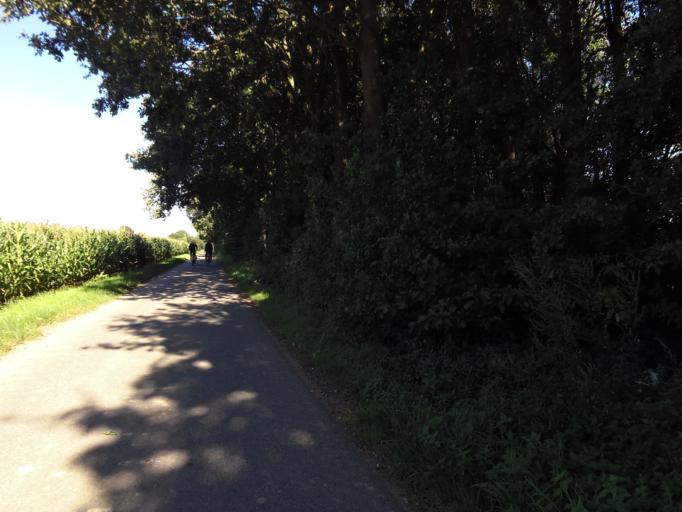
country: DE
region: North Rhine-Westphalia
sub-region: Regierungsbezirk Koln
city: Rheinbach
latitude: 50.6475
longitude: 6.9237
